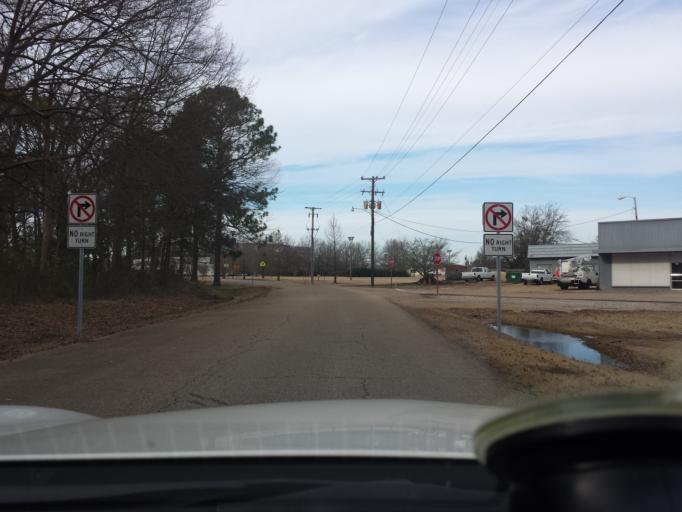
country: US
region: Mississippi
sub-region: Lee County
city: Tupelo
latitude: 34.2372
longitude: -88.7117
